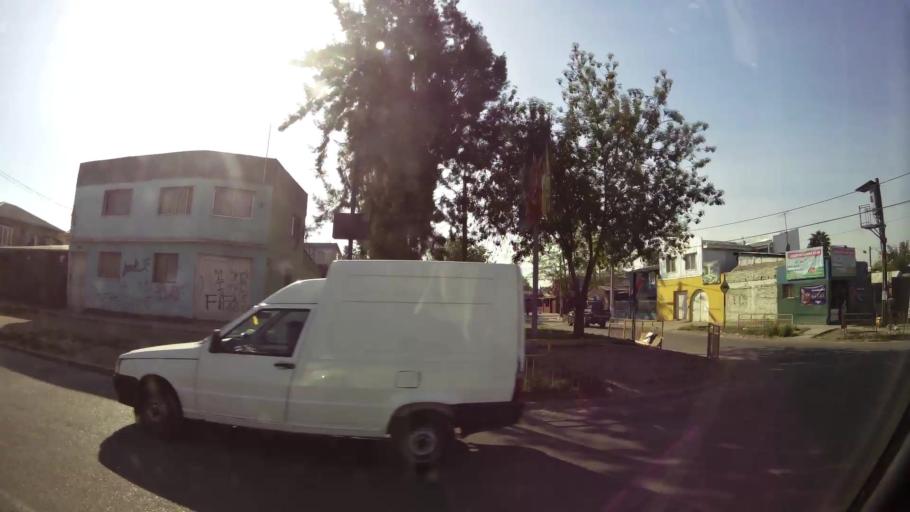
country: CL
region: Santiago Metropolitan
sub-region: Provincia de Santiago
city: Lo Prado
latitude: -33.4201
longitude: -70.7475
